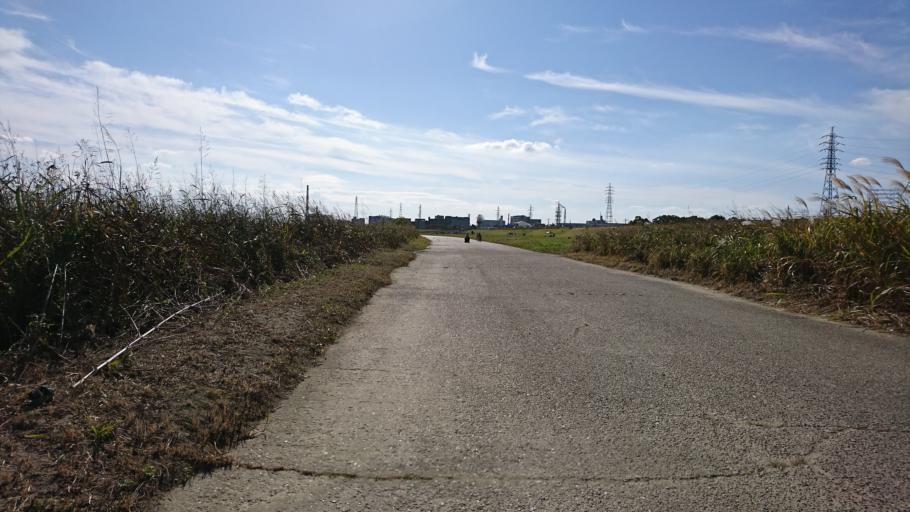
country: JP
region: Hyogo
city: Kakogawacho-honmachi
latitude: 34.7611
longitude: 134.8061
